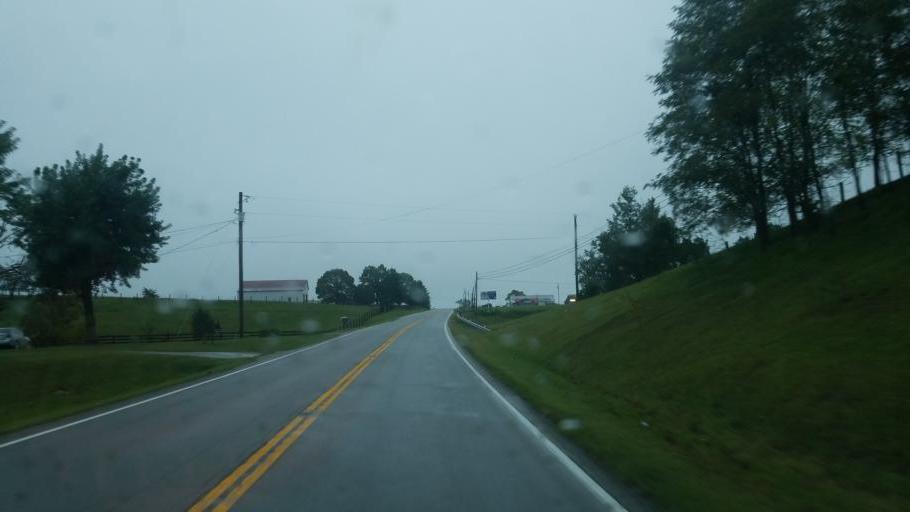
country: US
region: Kentucky
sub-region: Fleming County
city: Flemingsburg
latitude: 38.3883
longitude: -83.6694
